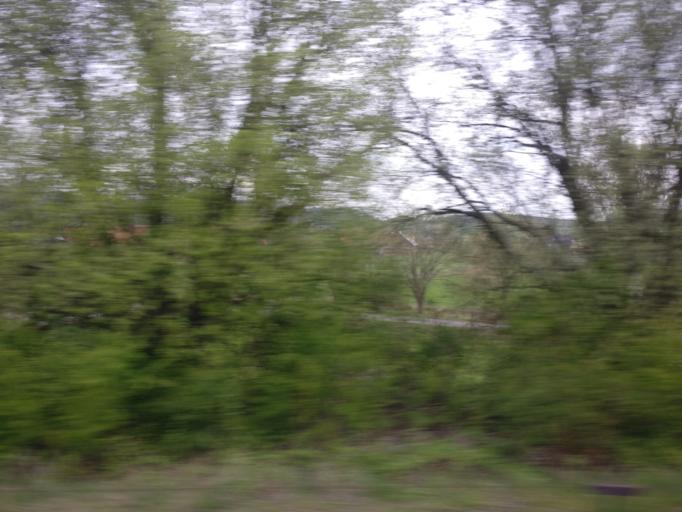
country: DE
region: Lower Saxony
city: Liebenburg
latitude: 52.0041
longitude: 10.3886
